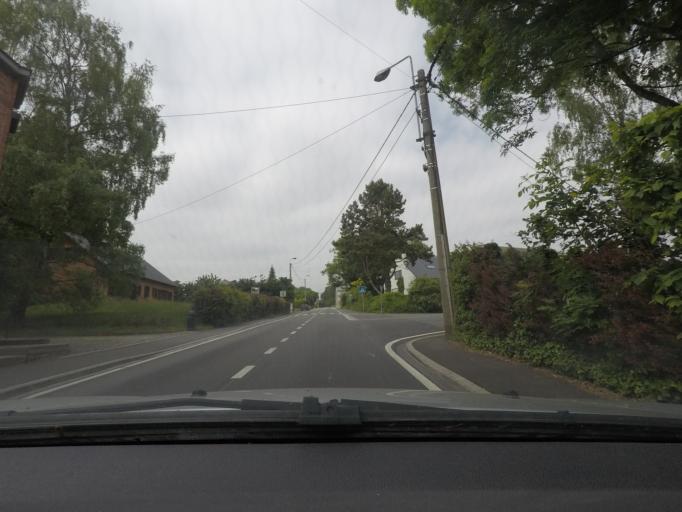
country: BE
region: Wallonia
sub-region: Province de Namur
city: Noville-les-Bois
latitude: 50.4980
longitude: 5.0065
